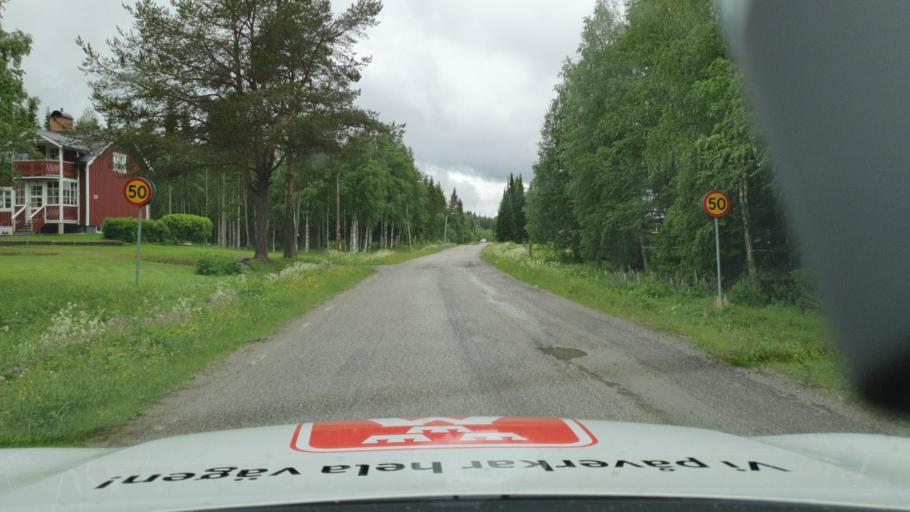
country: SE
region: Vaesterbotten
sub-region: Dorotea Kommun
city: Dorotea
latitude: 64.0940
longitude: 16.6558
